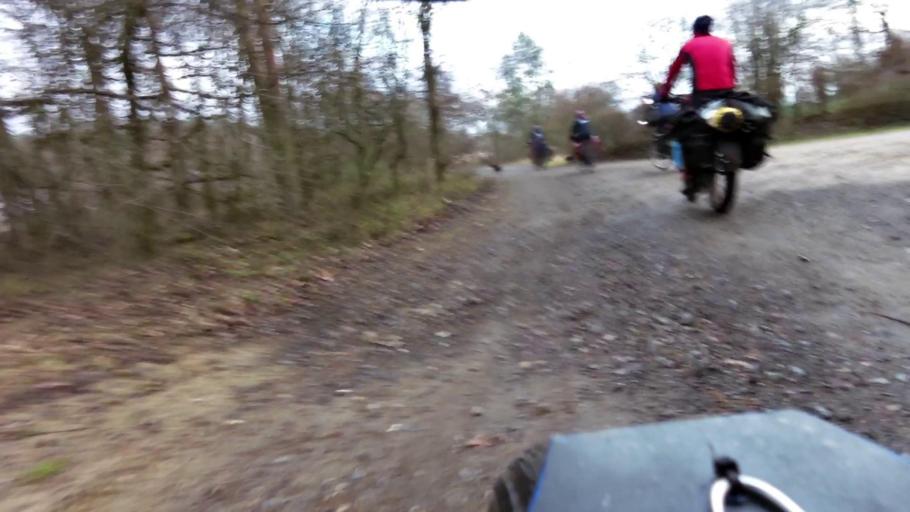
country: PL
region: Lubusz
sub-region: Powiat gorzowski
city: Jenin
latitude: 52.7109
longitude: 15.1302
